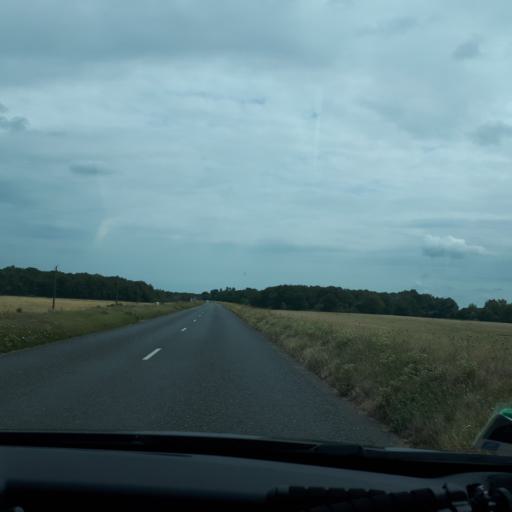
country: FR
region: Centre
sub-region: Departement du Loiret
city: Sully-sur-Loire
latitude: 47.7726
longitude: 2.4105
